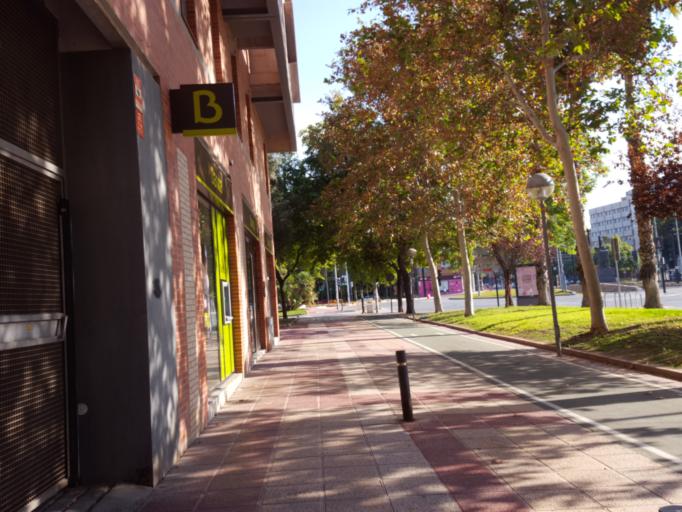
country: ES
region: Murcia
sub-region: Murcia
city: Murcia
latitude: 37.9944
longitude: -1.1243
